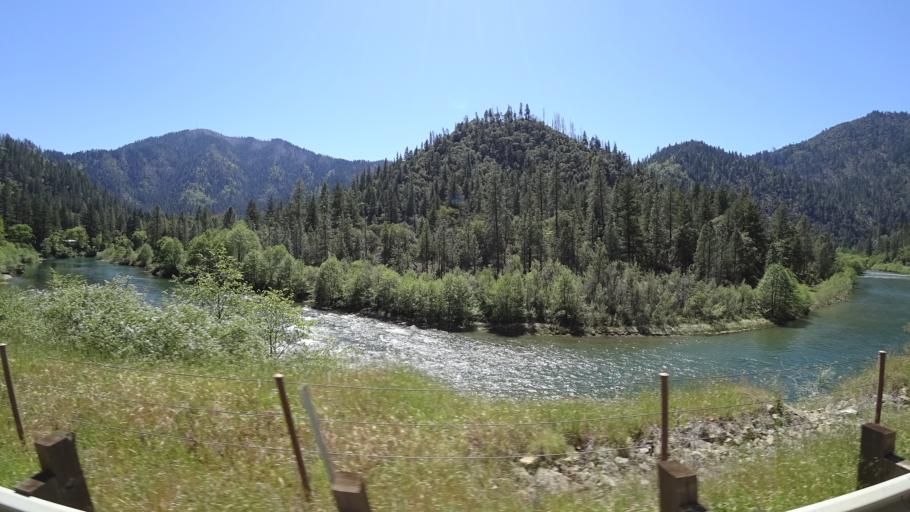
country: US
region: California
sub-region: Trinity County
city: Hayfork
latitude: 40.7845
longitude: -123.3366
